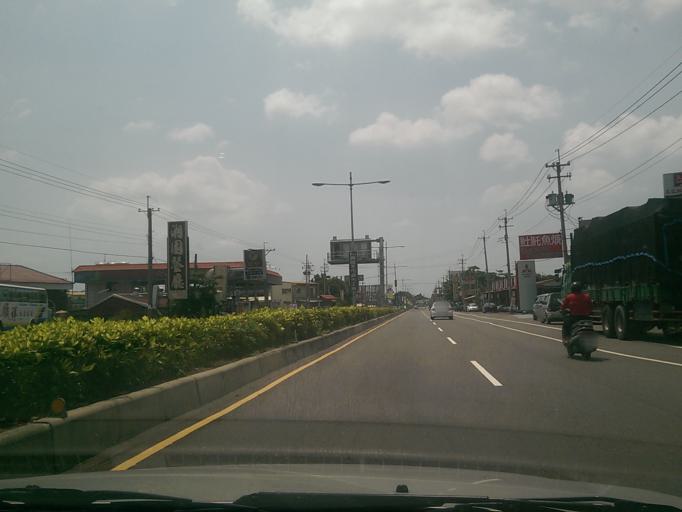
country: TW
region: Taiwan
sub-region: Yunlin
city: Douliu
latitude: 23.6937
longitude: 120.4690
